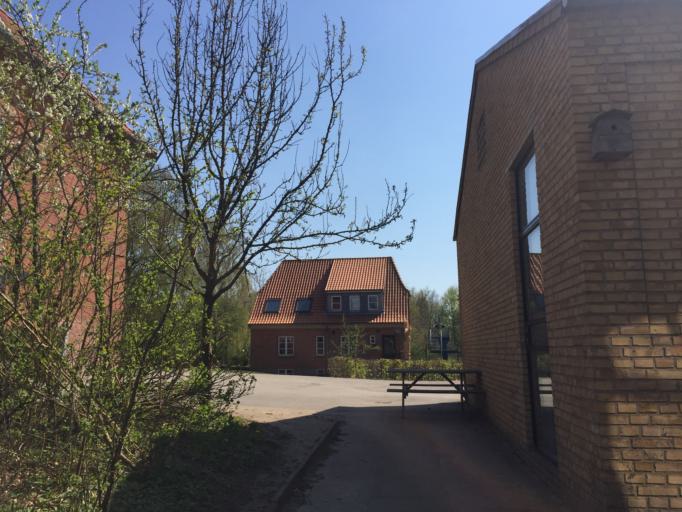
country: DK
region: South Denmark
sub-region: Vejle Kommune
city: Jelling
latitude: 55.7551
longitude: 9.4224
